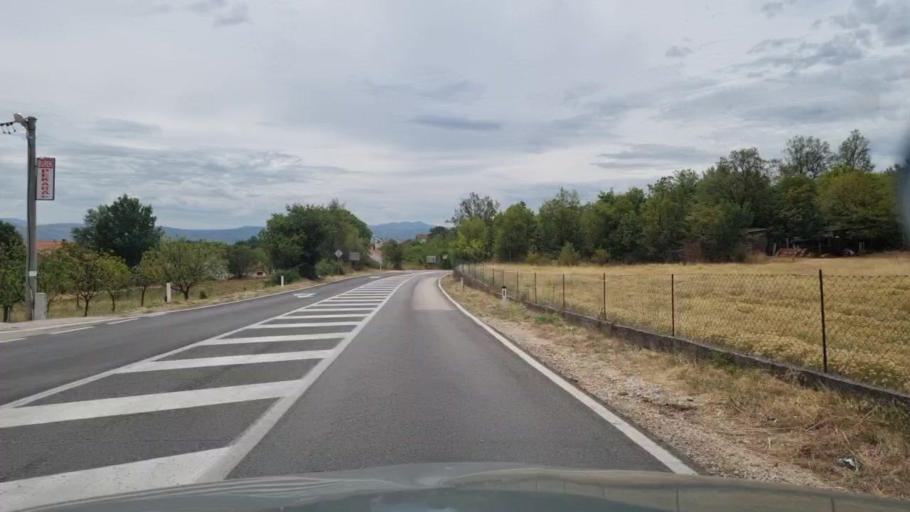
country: BA
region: Federation of Bosnia and Herzegovina
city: Crnici
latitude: 43.1085
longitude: 17.9045
